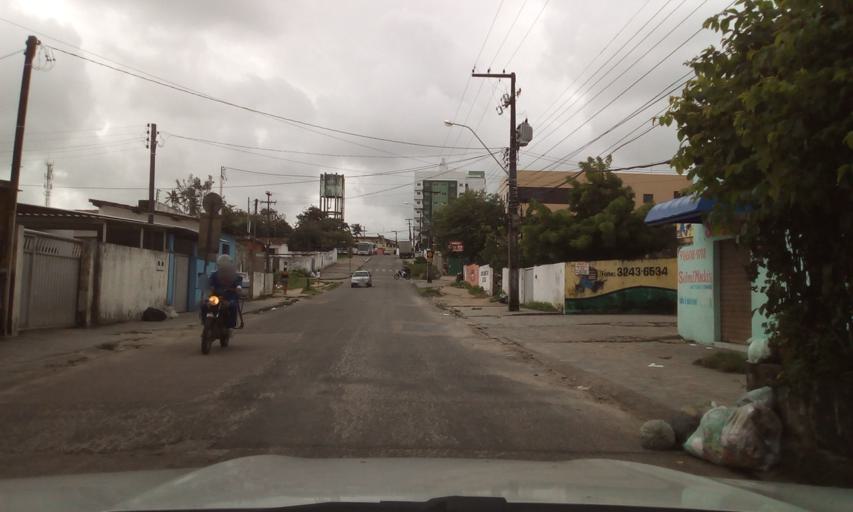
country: BR
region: Paraiba
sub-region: Joao Pessoa
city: Joao Pessoa
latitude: -7.1004
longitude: -34.8653
